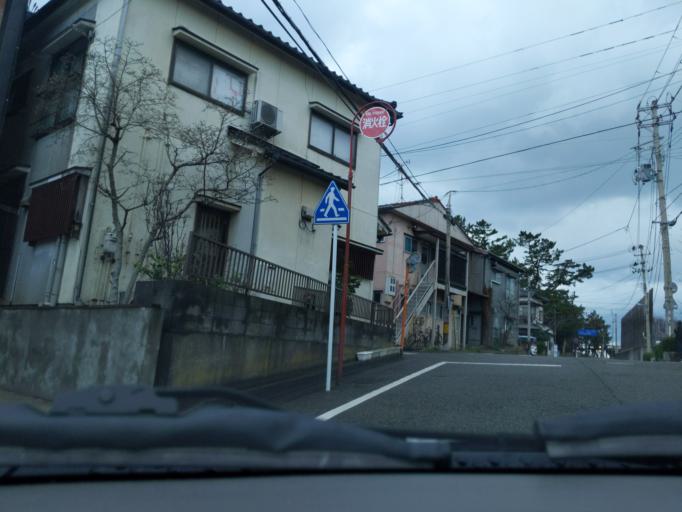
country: JP
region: Niigata
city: Niigata-shi
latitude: 37.9285
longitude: 139.0385
